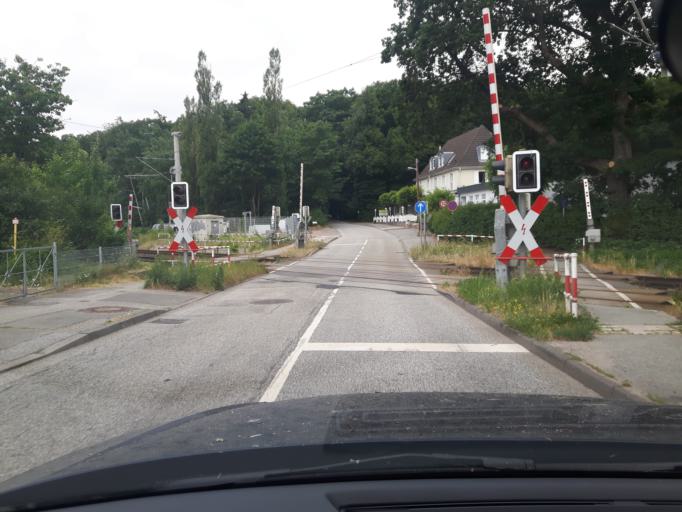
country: DE
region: Schleswig-Holstein
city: Ratekau
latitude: 53.9157
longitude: 10.7941
